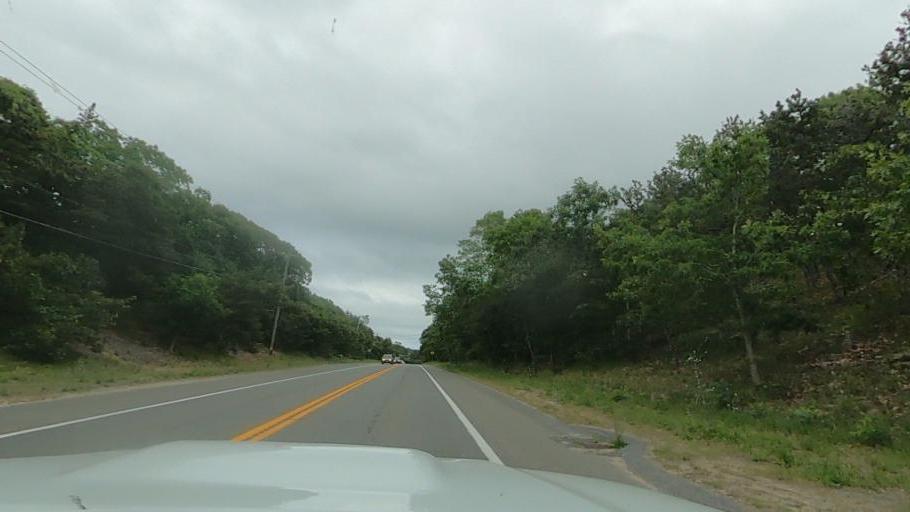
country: US
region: Massachusetts
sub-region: Barnstable County
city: Wellfleet
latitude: 41.9441
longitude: -70.0289
